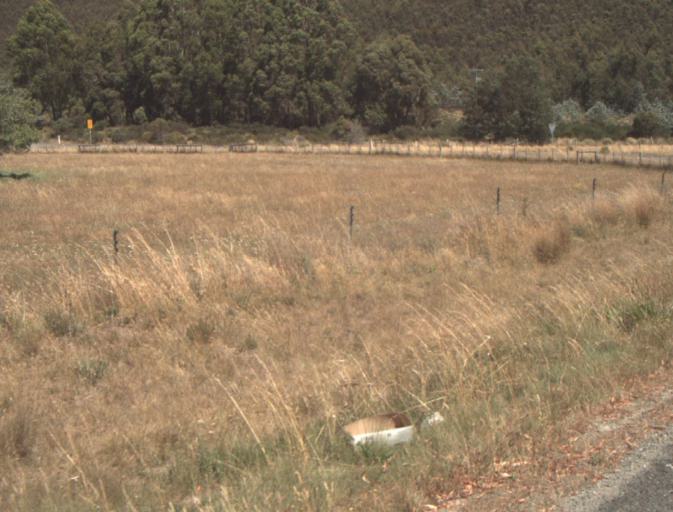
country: AU
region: Tasmania
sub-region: Dorset
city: Scottsdale
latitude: -41.3106
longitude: 147.3758
